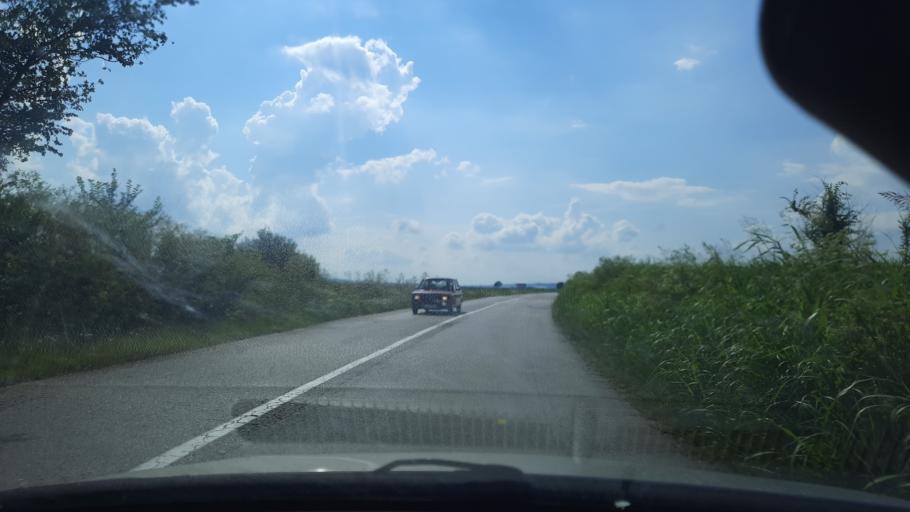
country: RS
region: Central Serbia
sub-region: Branicevski Okrug
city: Malo Crnice
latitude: 44.5805
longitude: 21.3185
